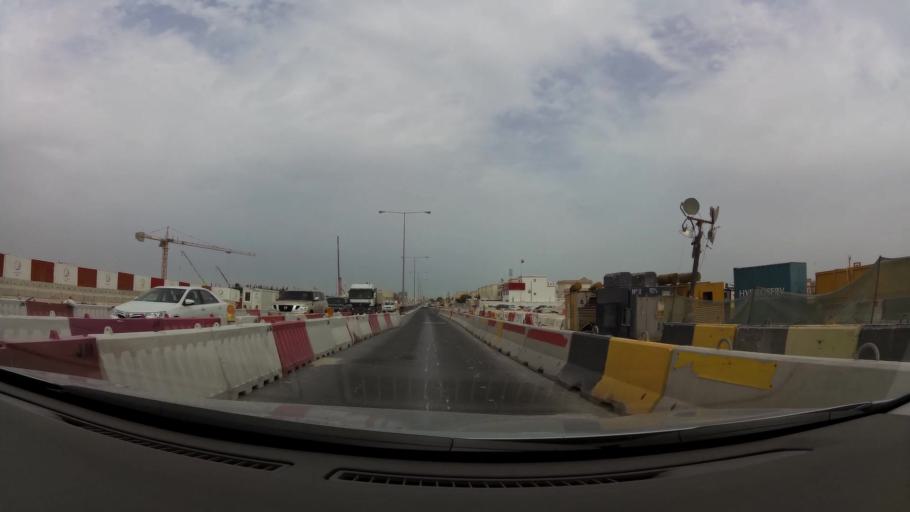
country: QA
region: Baladiyat ar Rayyan
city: Ar Rayyan
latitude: 25.3538
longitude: 51.4623
